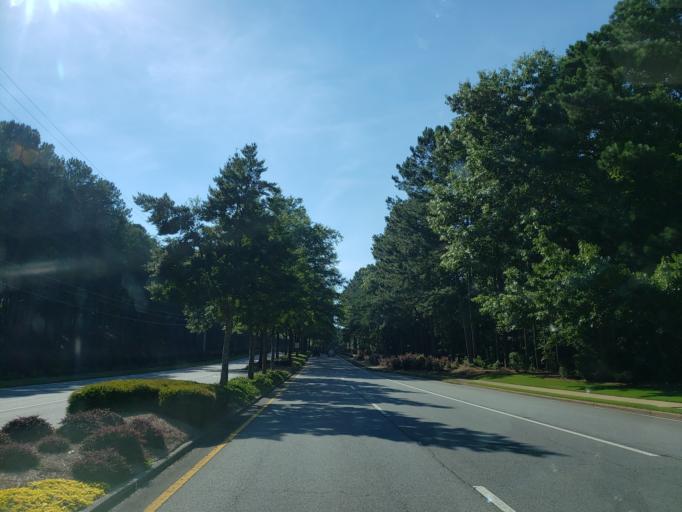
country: US
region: Georgia
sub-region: Cherokee County
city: Woodstock
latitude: 34.1217
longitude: -84.5552
